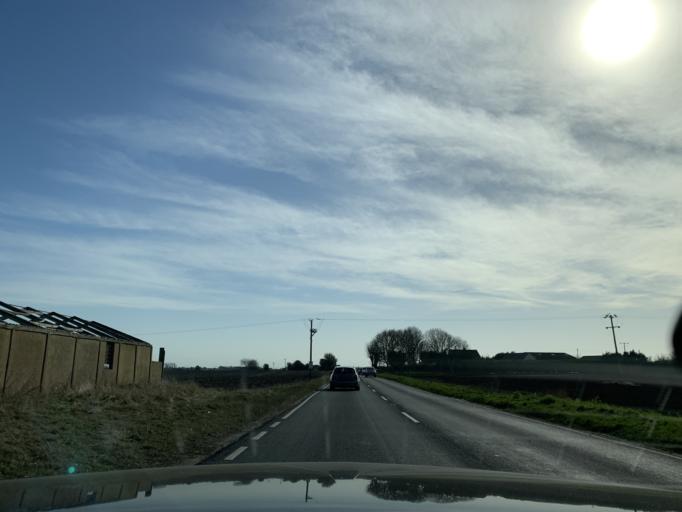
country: GB
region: England
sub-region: Kent
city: New Romney
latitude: 50.9808
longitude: 0.9211
